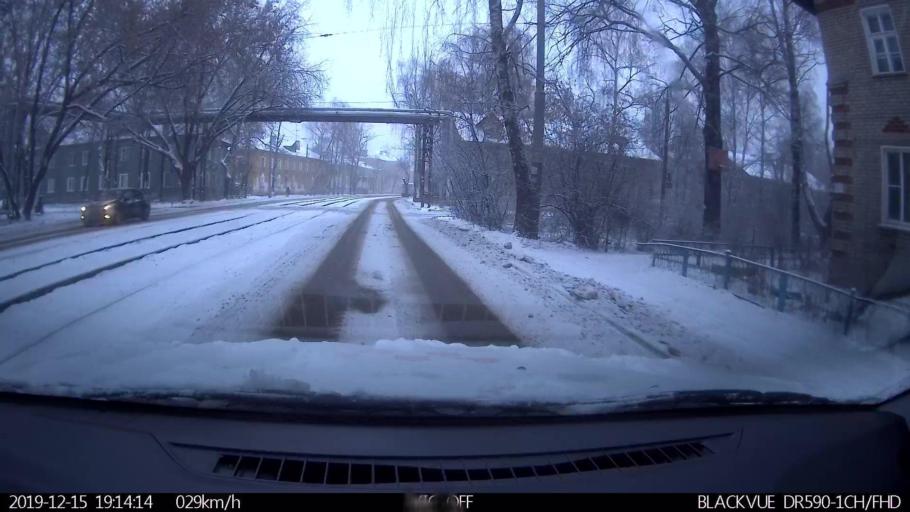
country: RU
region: Nizjnij Novgorod
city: Gorbatovka
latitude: 56.3500
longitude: 43.8449
